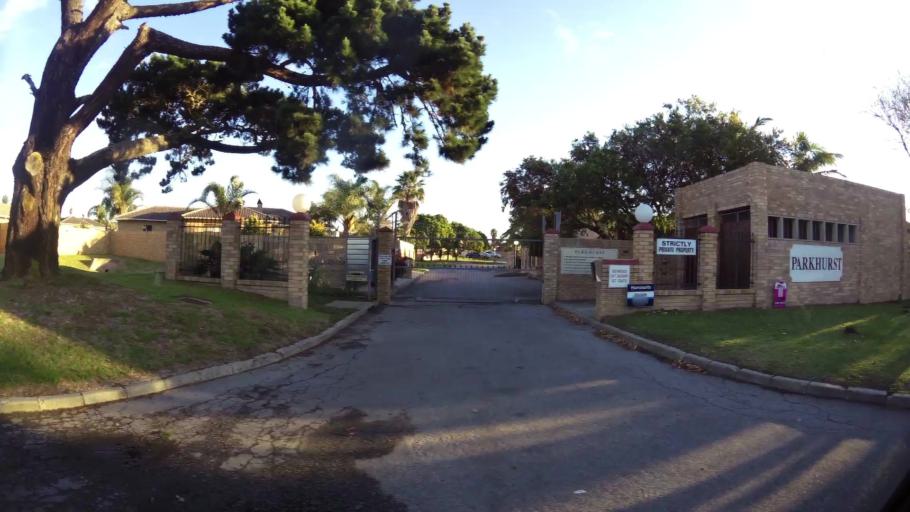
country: ZA
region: Eastern Cape
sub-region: Nelson Mandela Bay Metropolitan Municipality
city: Port Elizabeth
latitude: -33.9709
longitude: 25.4958
